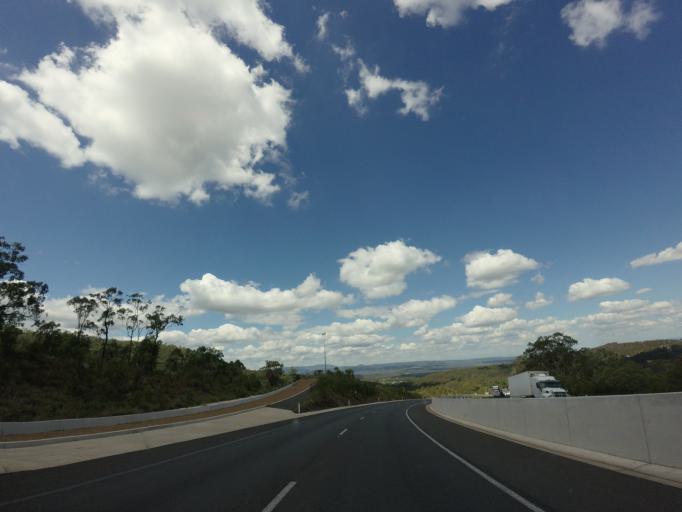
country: AU
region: Queensland
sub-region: Toowoomba
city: East Toowoomba
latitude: -27.5699
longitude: 151.9890
